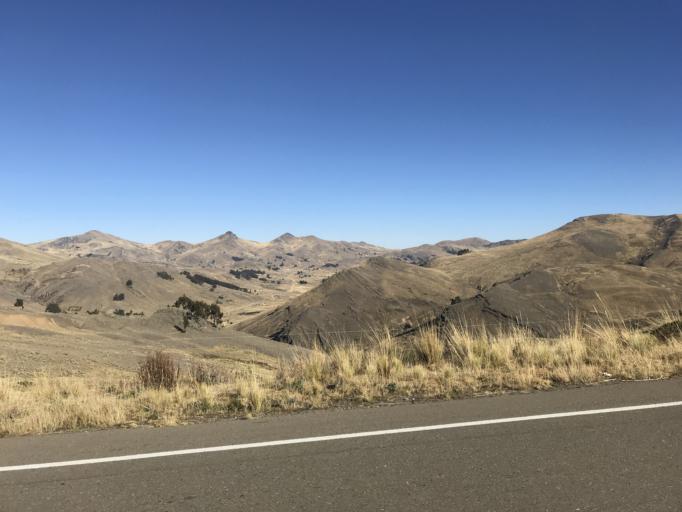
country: PE
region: Puno
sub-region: Yunguyo
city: Yunguyo
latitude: -16.1828
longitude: -68.9817
